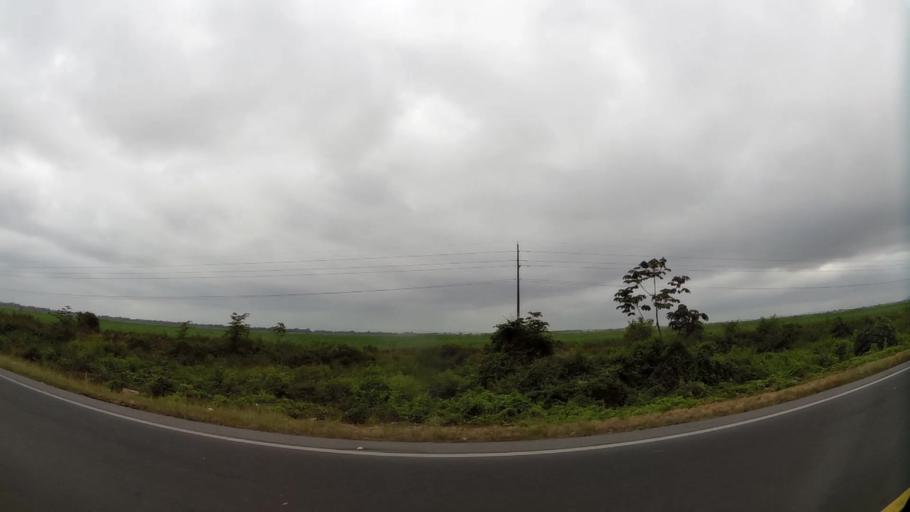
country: EC
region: Guayas
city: Naranjito
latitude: -2.3230
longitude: -79.6367
